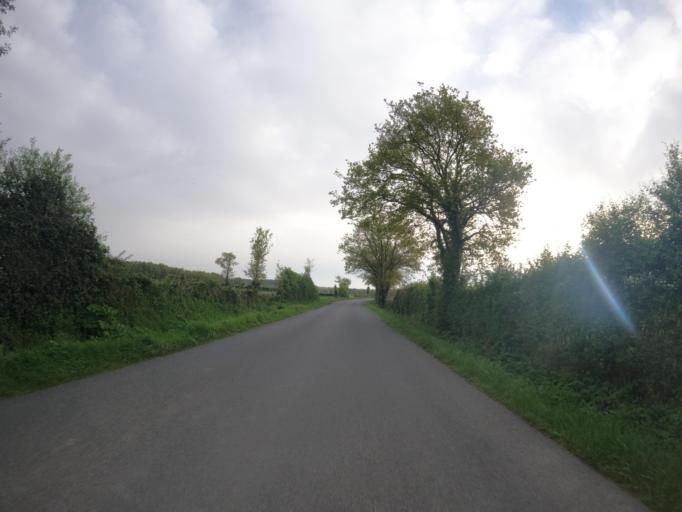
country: FR
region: Poitou-Charentes
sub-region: Departement des Deux-Sevres
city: Moncoutant
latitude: 46.6992
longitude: -0.5350
